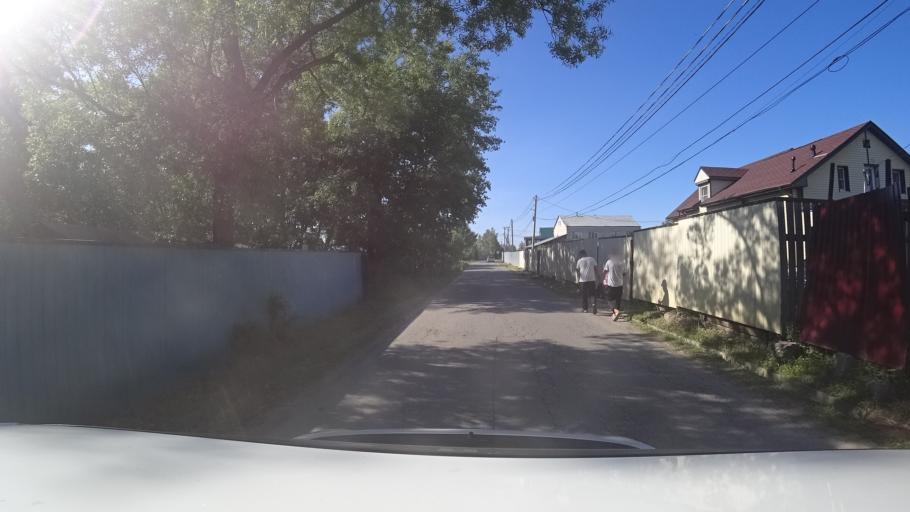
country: RU
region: Khabarovsk Krai
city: Topolevo
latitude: 48.5427
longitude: 135.1741
